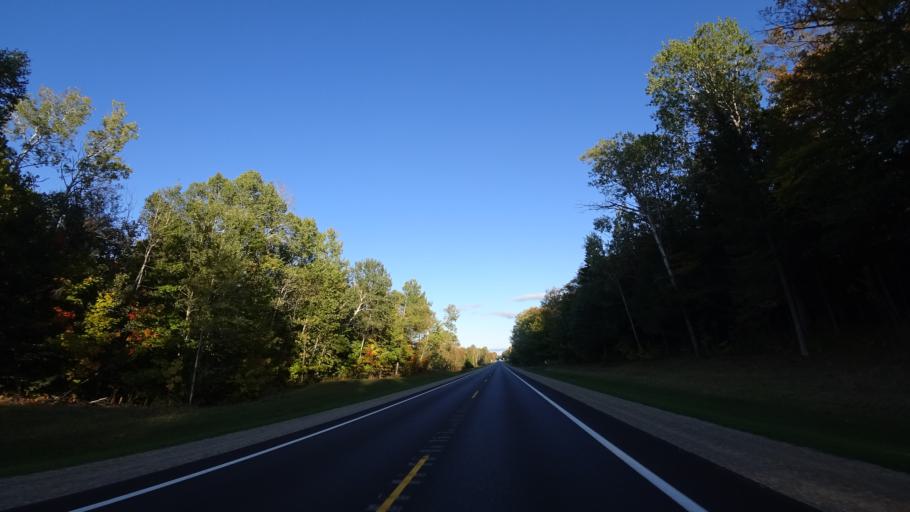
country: US
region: Michigan
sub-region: Luce County
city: Newberry
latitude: 46.3392
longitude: -85.7108
